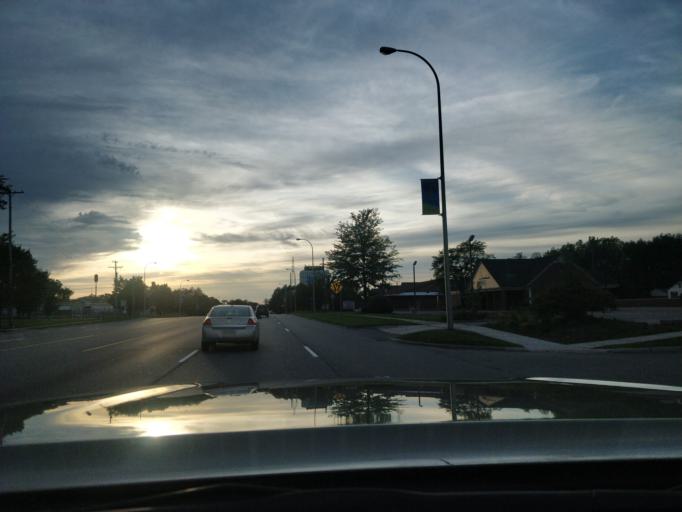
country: US
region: Michigan
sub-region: Wayne County
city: Southgate
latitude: 42.1987
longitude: -83.2298
